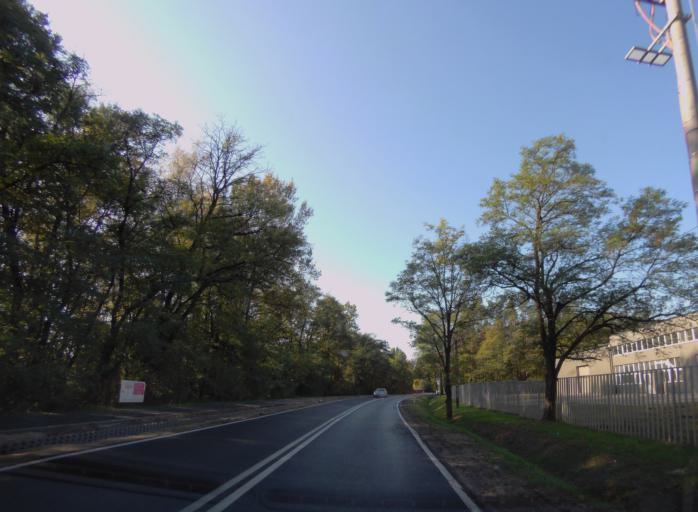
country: PL
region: Masovian Voivodeship
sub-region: Powiat minski
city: Halinow
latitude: 52.1980
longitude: 21.3757
